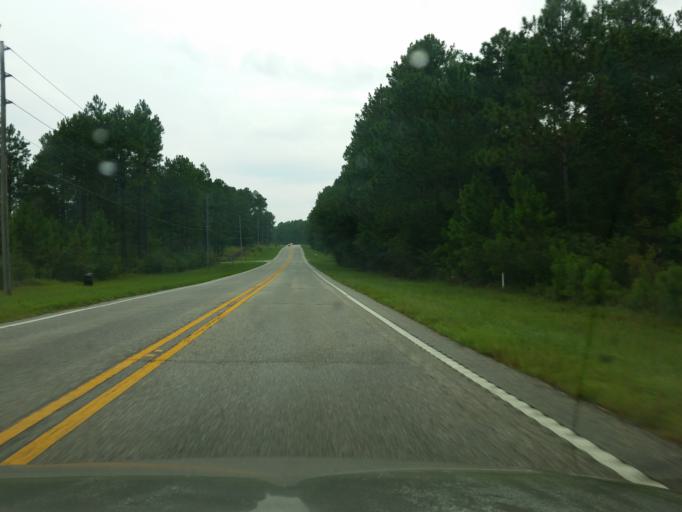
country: US
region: Alabama
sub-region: Baldwin County
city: Elberta
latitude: 30.5283
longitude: -87.5147
